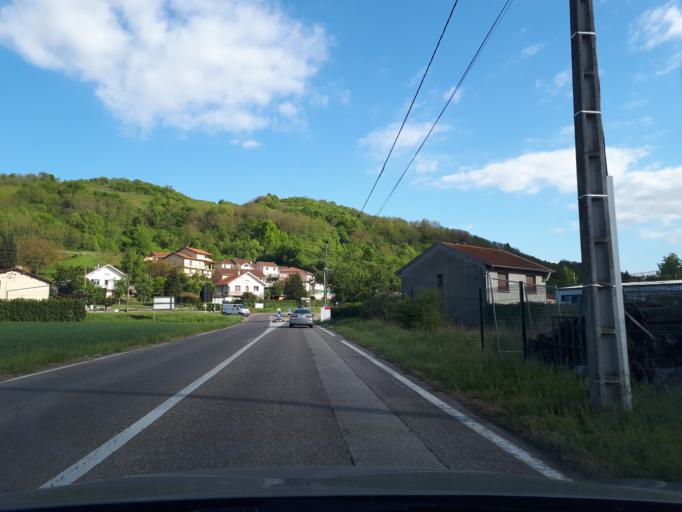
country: FR
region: Rhone-Alpes
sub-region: Departement de l'Isere
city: Bourgoin-Jallieu
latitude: 45.6130
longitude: 5.2733
